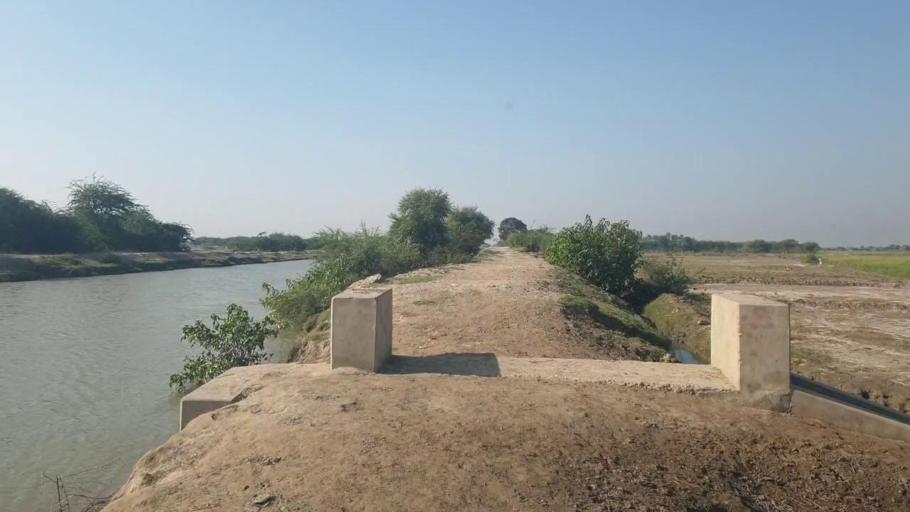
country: PK
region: Sindh
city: Badin
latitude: 24.7063
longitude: 68.8866
